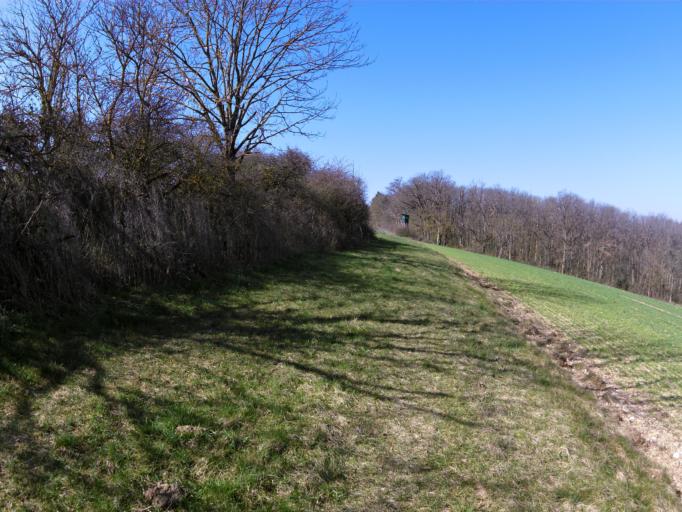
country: DE
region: Bavaria
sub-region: Regierungsbezirk Unterfranken
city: Erlabrunn
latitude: 49.8526
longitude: 9.8294
